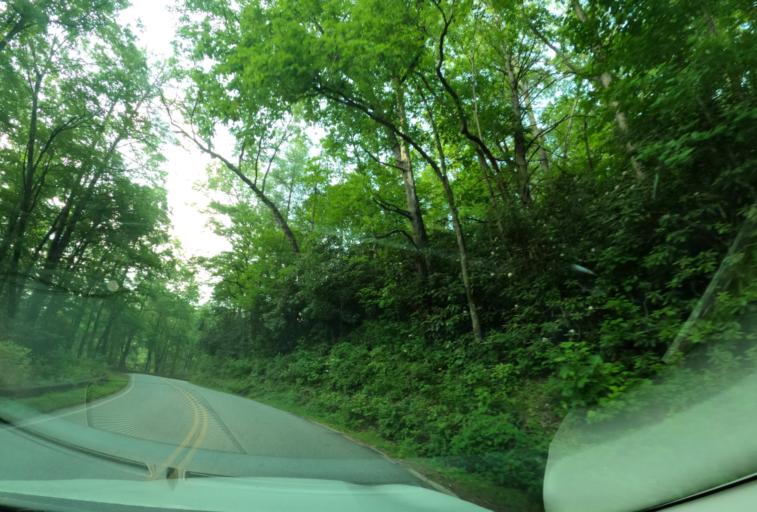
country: US
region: North Carolina
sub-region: Transylvania County
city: Brevard
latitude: 35.1896
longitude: -82.8482
